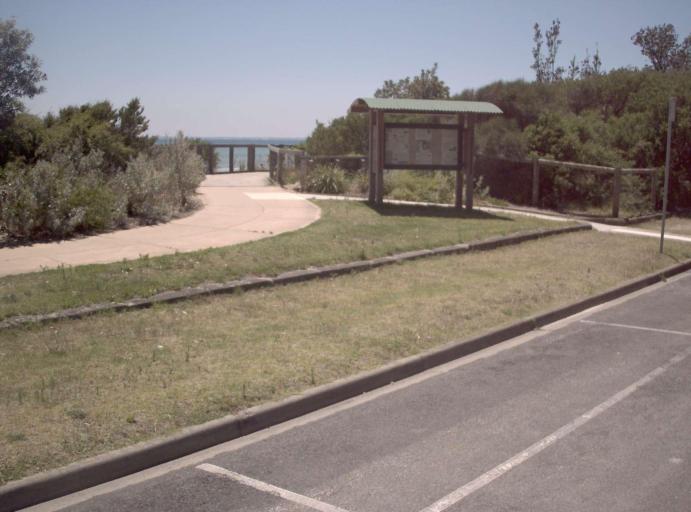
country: AU
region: Victoria
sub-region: Frankston
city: Frankston
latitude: -38.1518
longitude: 145.1130
